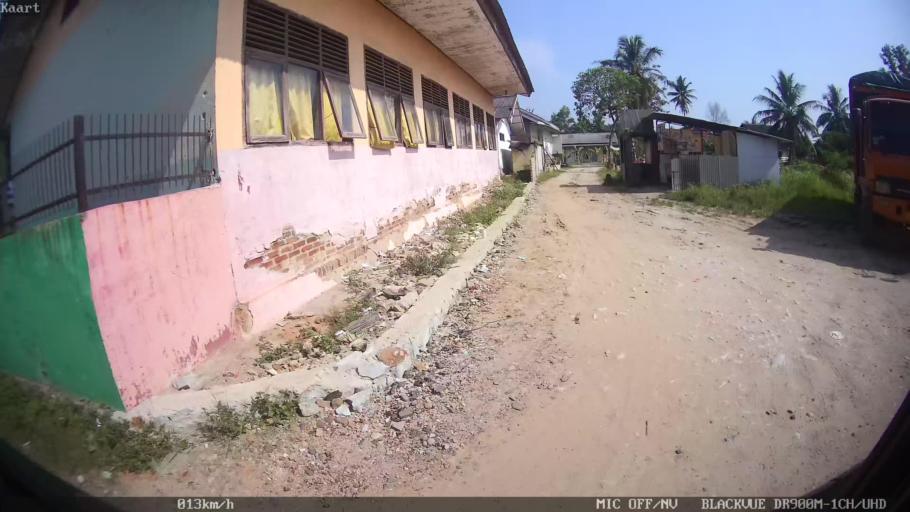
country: ID
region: Lampung
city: Natar
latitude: -5.2567
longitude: 105.1852
